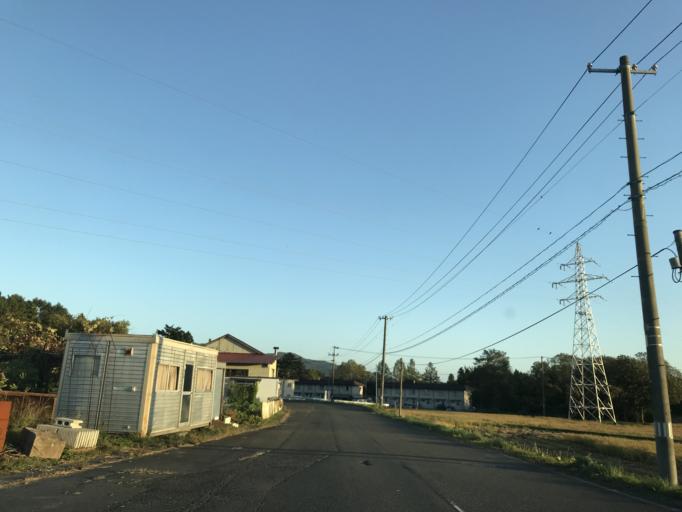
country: JP
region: Iwate
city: Mizusawa
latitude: 39.0525
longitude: 141.1174
